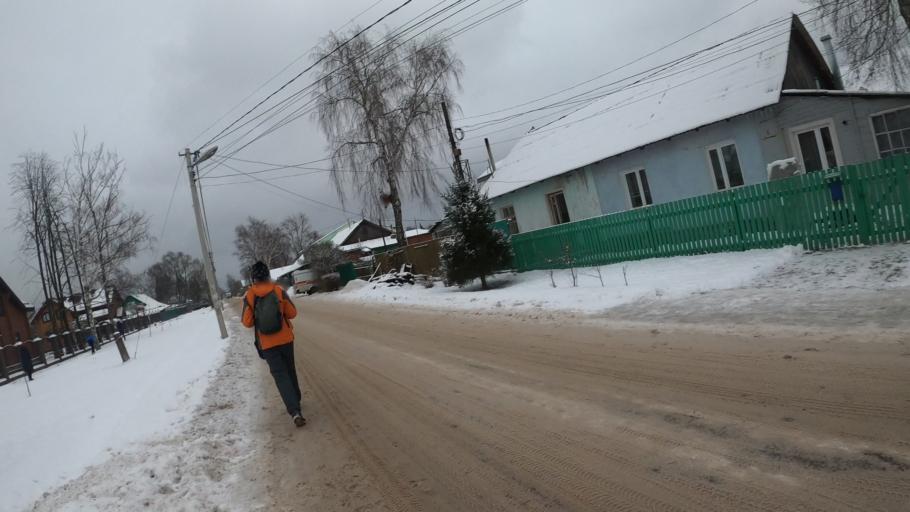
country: RU
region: Jaroslavl
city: Pereslavl'-Zalesskiy
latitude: 56.7292
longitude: 38.8365
